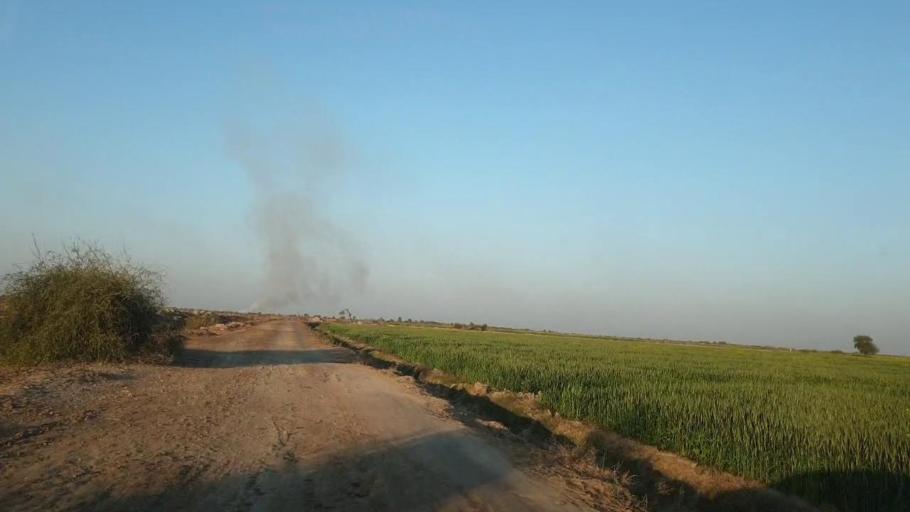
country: PK
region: Sindh
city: Mirpur Khas
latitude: 25.7068
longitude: 69.0433
